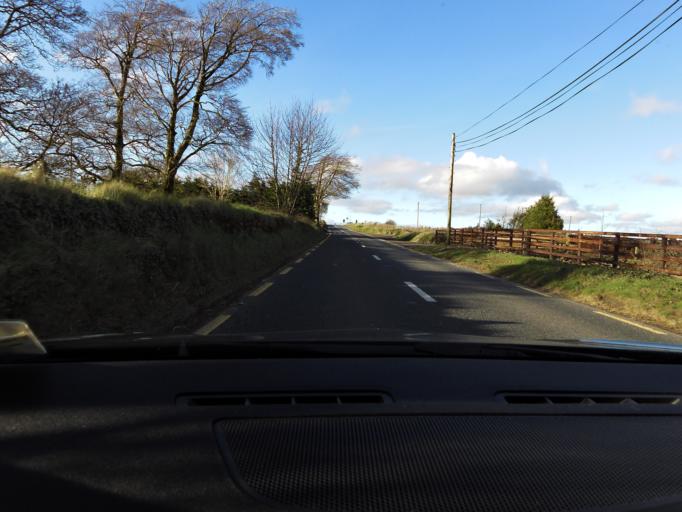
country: IE
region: Connaught
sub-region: Roscommon
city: Roscommon
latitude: 53.6593
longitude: -8.1982
